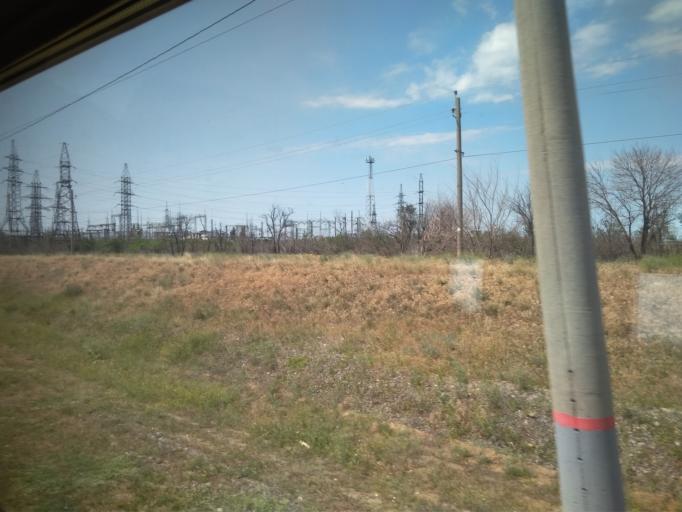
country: RU
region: Volgograd
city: Gumrak
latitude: 48.7601
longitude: 44.4269
